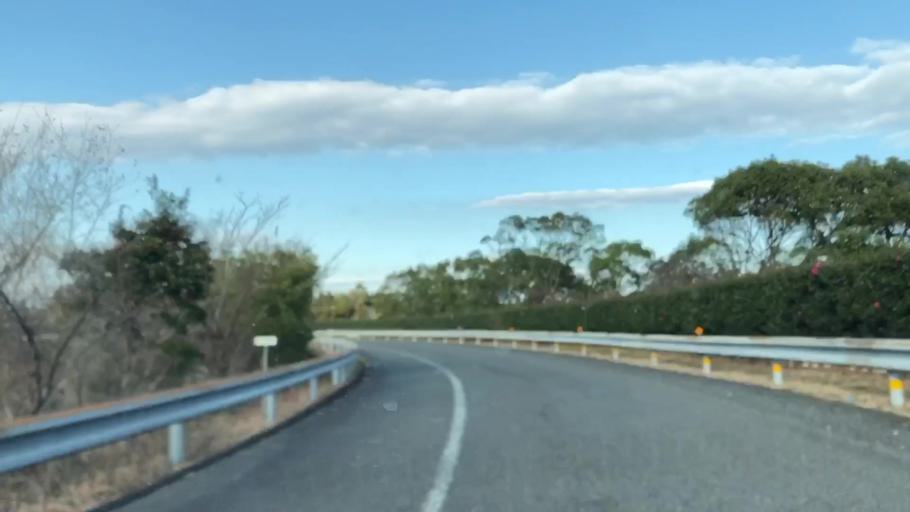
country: JP
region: Miyazaki
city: Miyazaki-shi
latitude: 31.8701
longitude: 131.4144
